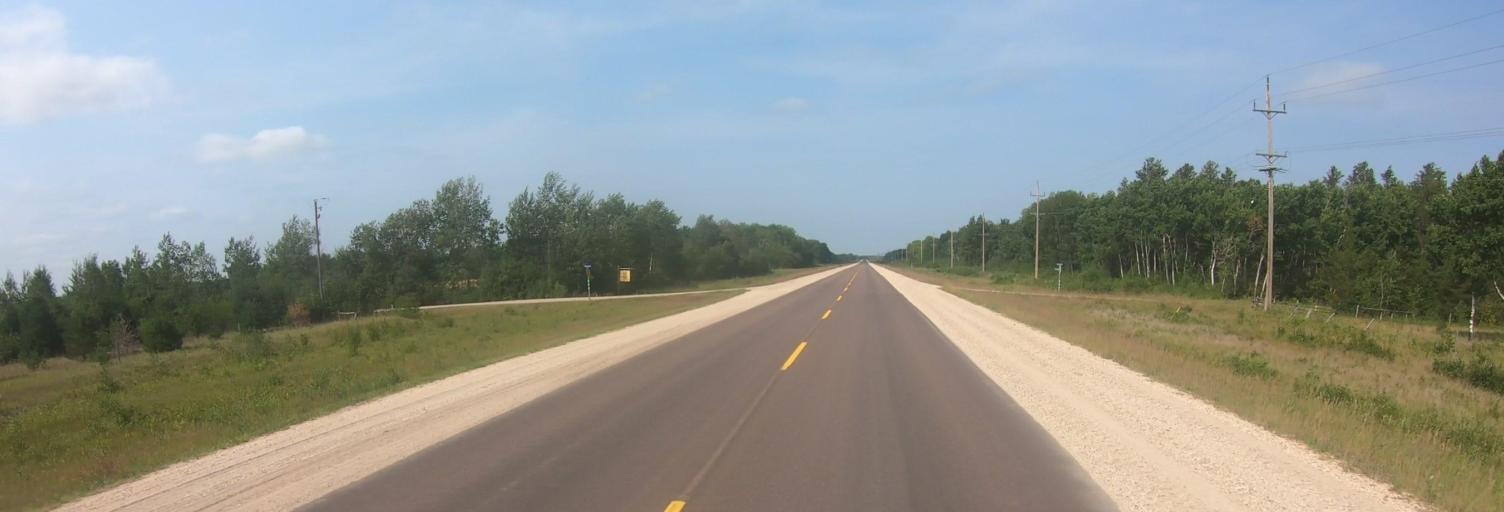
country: CA
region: Manitoba
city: La Broquerie
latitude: 49.2670
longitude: -96.4415
